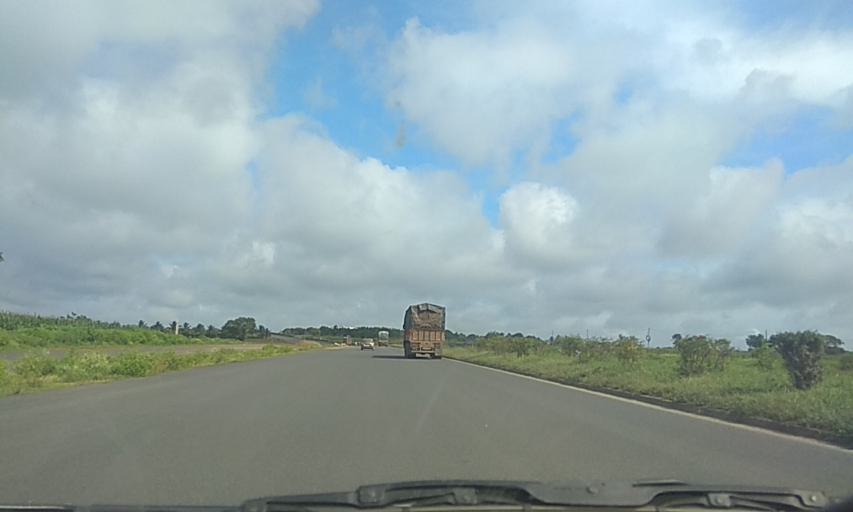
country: IN
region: Karnataka
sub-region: Haveri
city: Shiggaon
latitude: 15.0028
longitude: 75.2054
